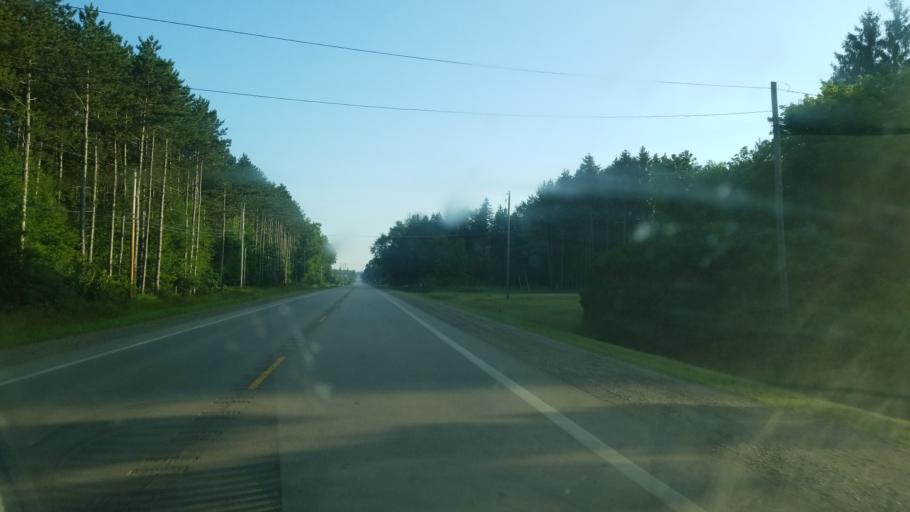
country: US
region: Michigan
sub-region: Montcalm County
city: Stanton
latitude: 43.2656
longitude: -85.0737
